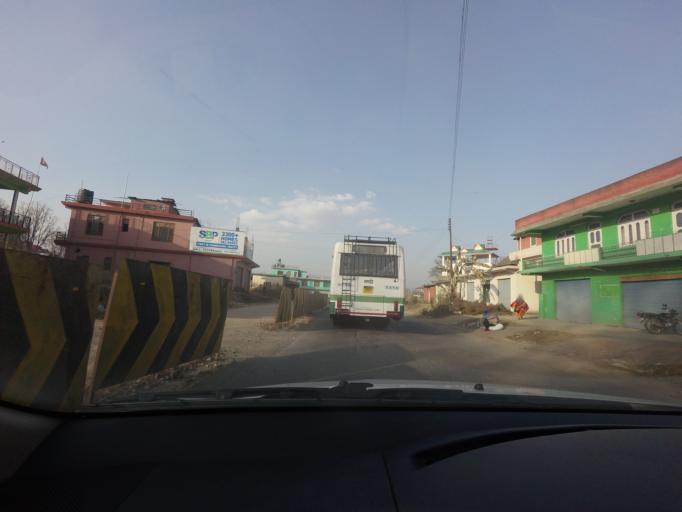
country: IN
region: Himachal Pradesh
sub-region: Mandi
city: Sundarnagar
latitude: 31.5657
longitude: 76.9050
